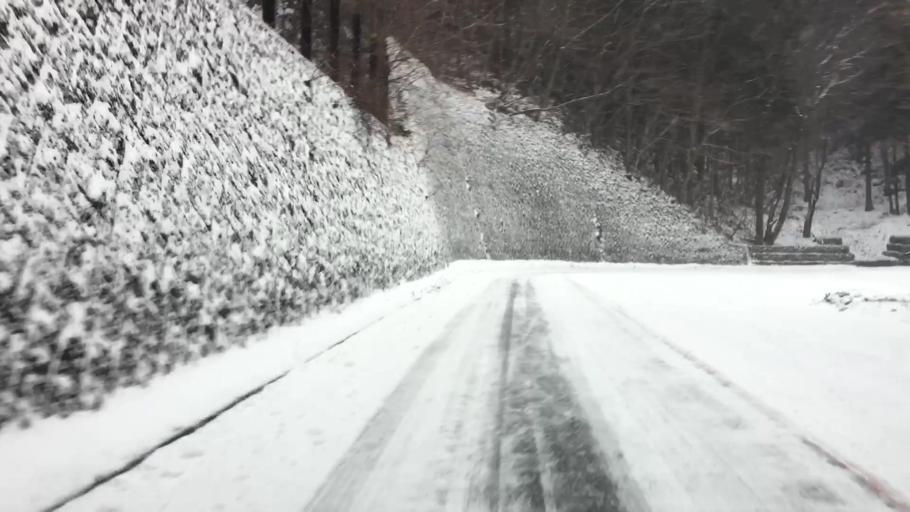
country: JP
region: Tochigi
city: Imaichi
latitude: 36.8721
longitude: 139.7209
